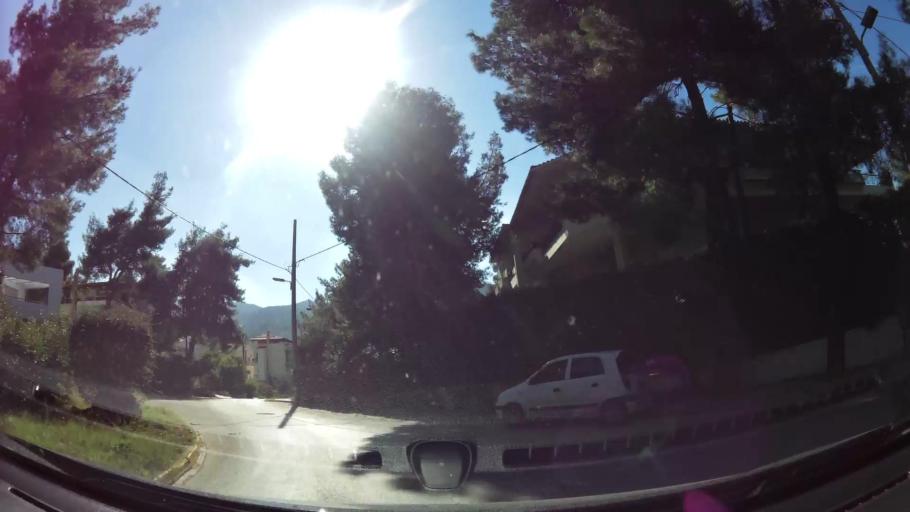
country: GR
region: Attica
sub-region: Nomarchia Anatolikis Attikis
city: Drosia
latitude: 38.1094
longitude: 23.8659
